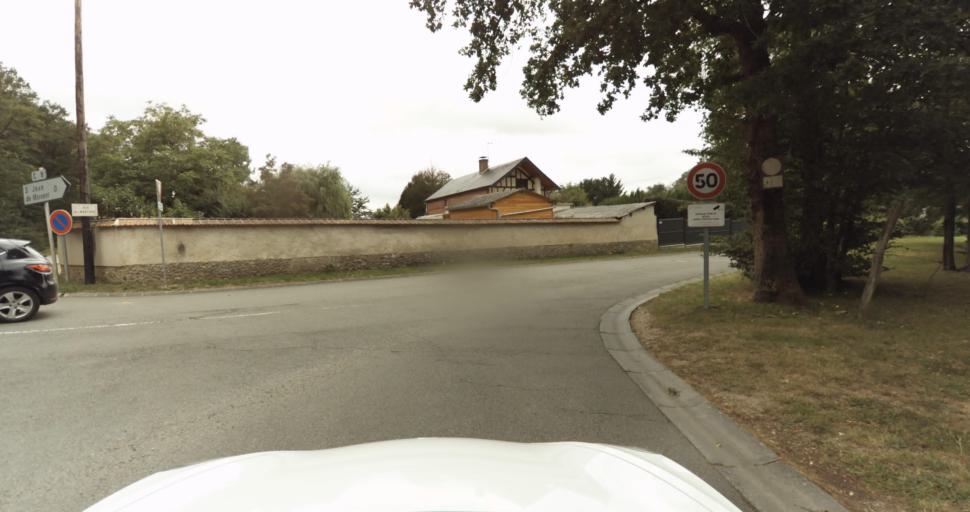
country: FR
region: Haute-Normandie
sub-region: Departement de l'Eure
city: Saint-Sebastien-de-Morsent
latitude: 49.0050
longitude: 1.0672
